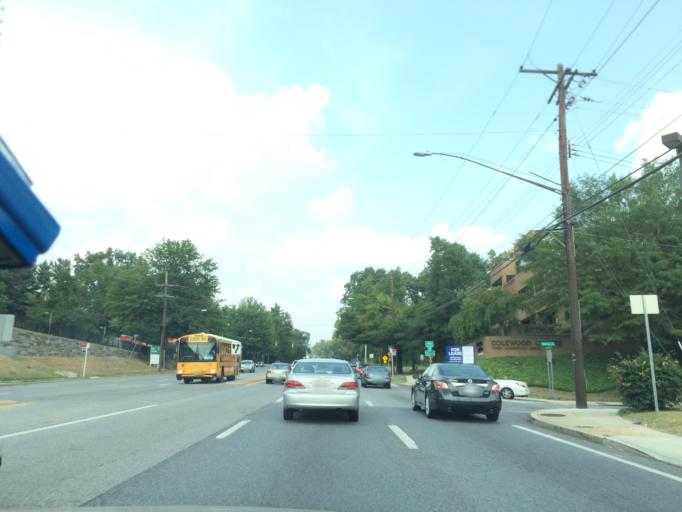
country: US
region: Maryland
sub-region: Montgomery County
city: White Oak
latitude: 39.0322
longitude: -77.0037
